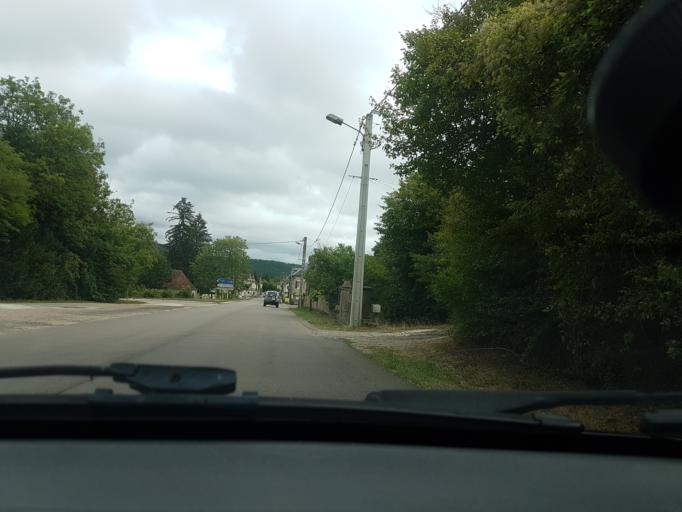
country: FR
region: Bourgogne
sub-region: Departement de l'Yonne
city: Joux-la-Ville
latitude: 47.5639
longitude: 3.7811
